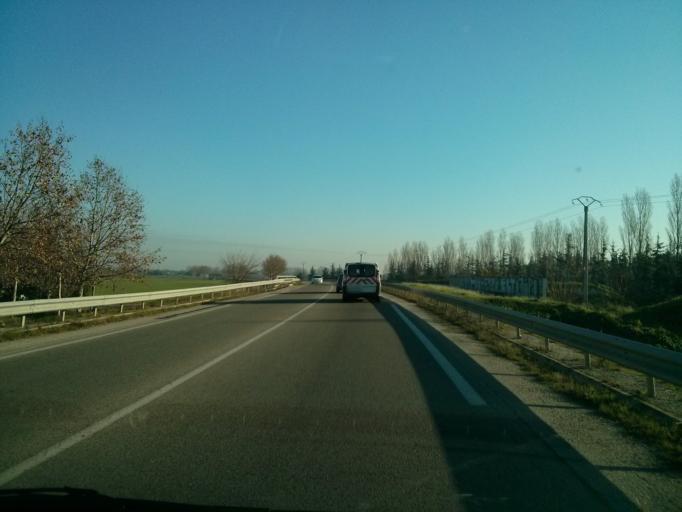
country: FR
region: Languedoc-Roussillon
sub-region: Departement du Gard
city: Vestric-et-Candiac
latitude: 43.7471
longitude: 4.2627
